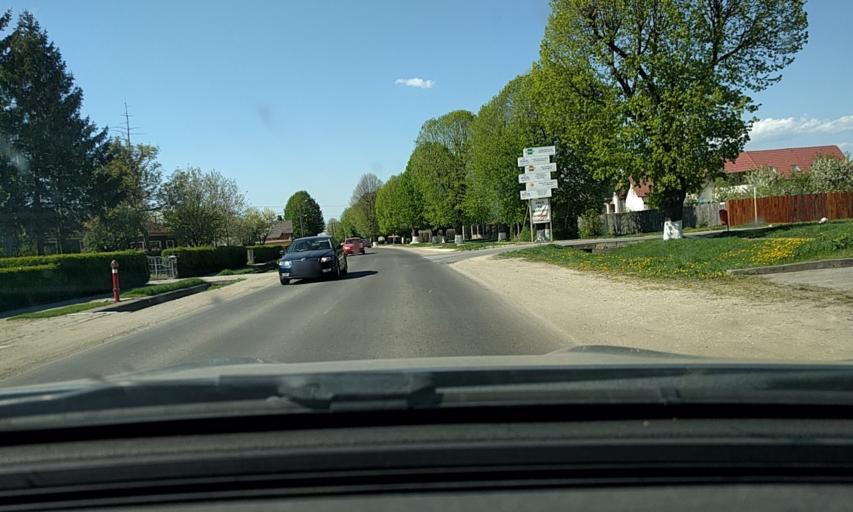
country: RO
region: Brasov
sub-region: Comuna Harman
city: Harman
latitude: 45.7075
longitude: 25.6870
